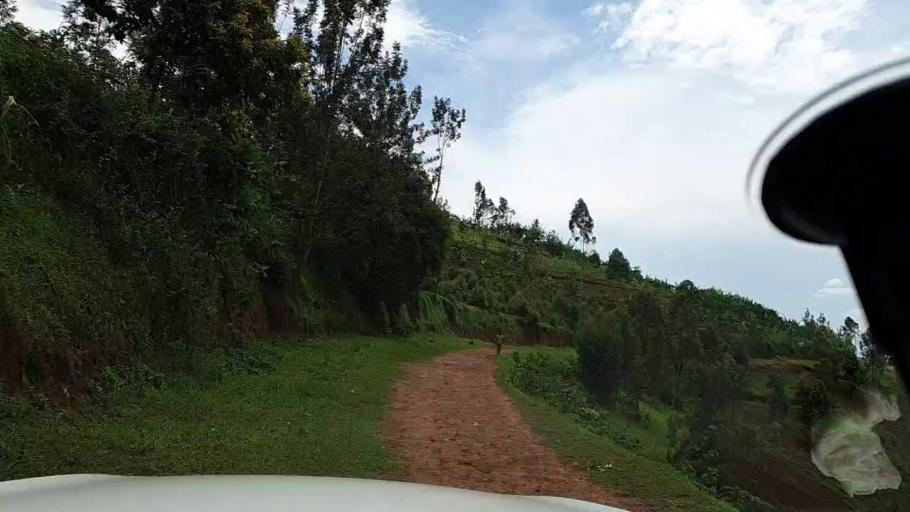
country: RW
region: Southern Province
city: Gitarama
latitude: -2.0655
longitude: 29.6455
